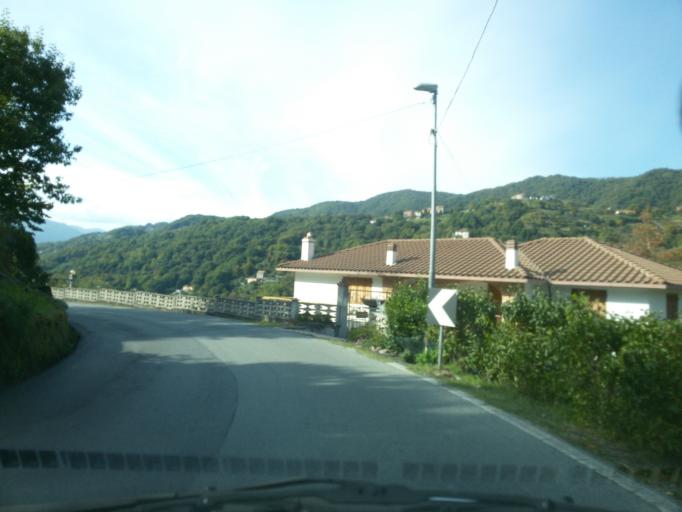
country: IT
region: Liguria
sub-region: Provincia di Genova
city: Piccarello
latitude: 44.4818
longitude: 8.9646
